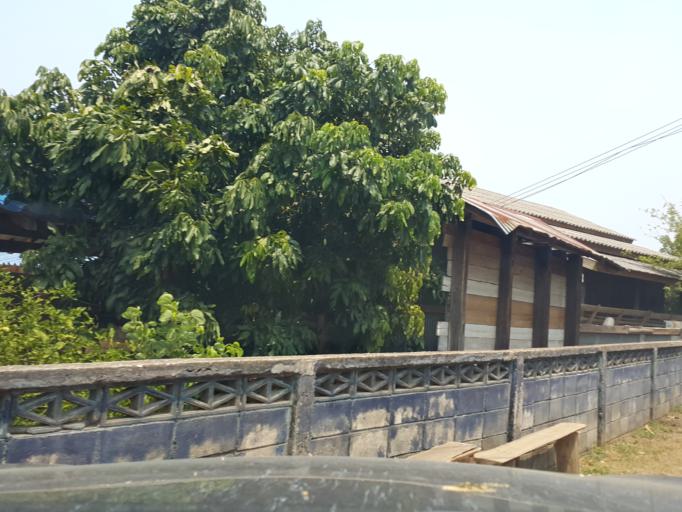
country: TH
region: Lampang
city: Mae Phrik
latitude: 17.5735
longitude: 99.0857
